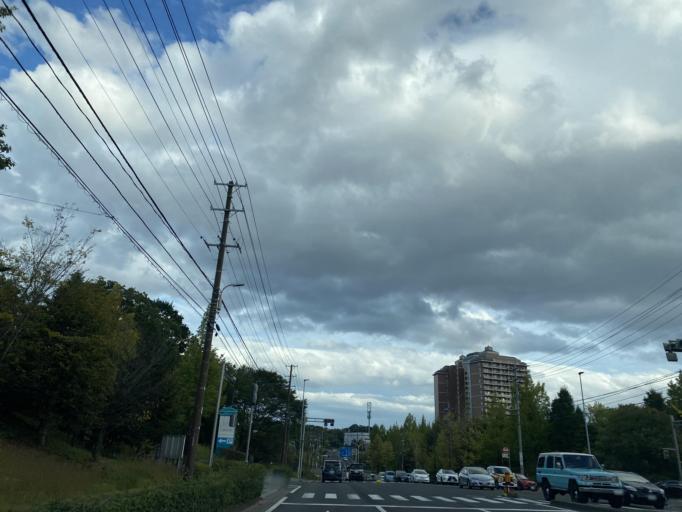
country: JP
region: Miyagi
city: Tomiya
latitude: 38.3440
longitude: 140.8368
